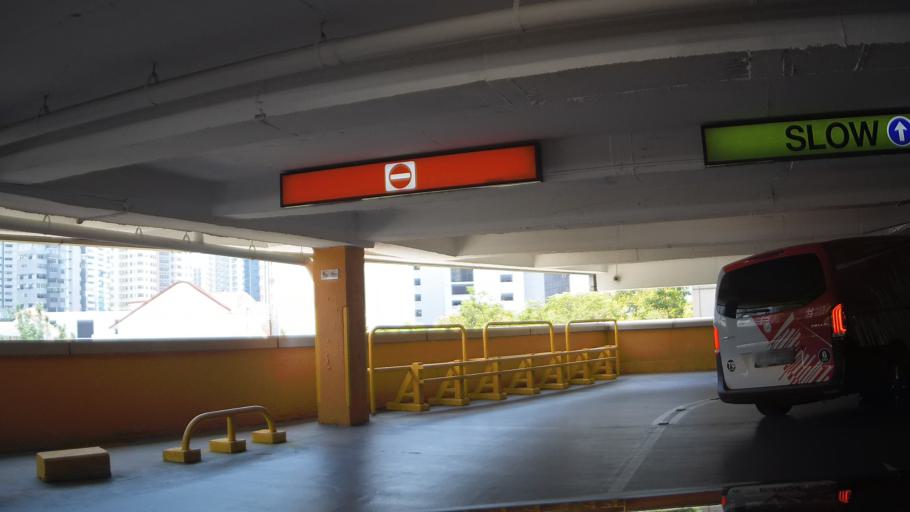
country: SG
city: Singapore
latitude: 1.2607
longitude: 103.8419
